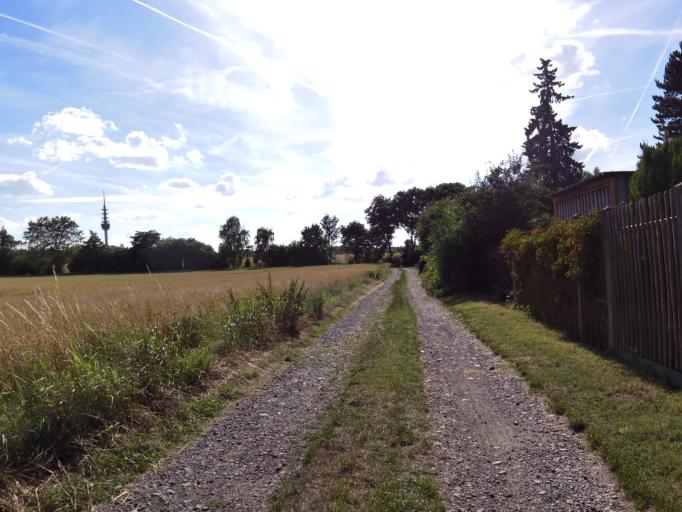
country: DE
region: Saxony
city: Taucha
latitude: 51.3222
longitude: 12.4588
